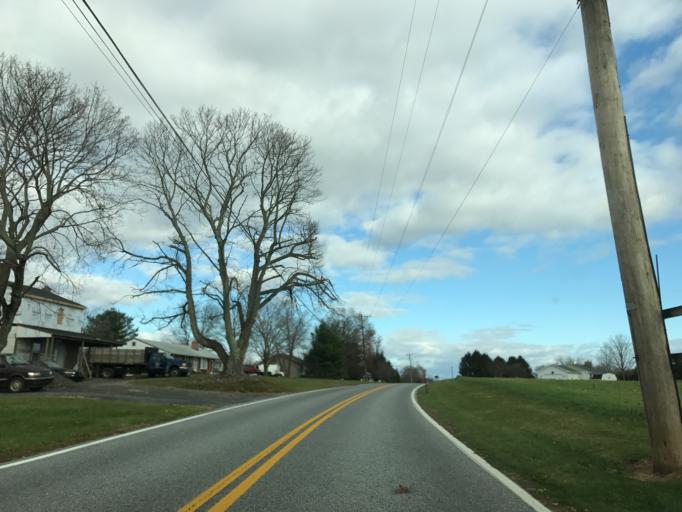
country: US
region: Pennsylvania
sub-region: York County
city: Stewartstown
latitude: 39.6670
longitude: -76.5964
